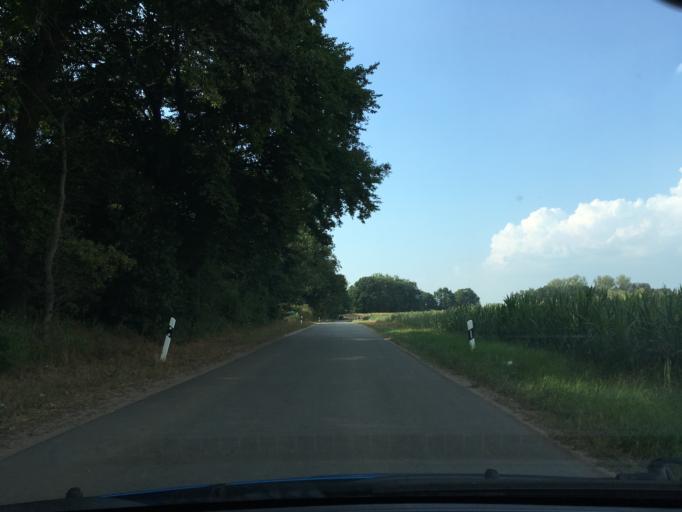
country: DE
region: Lower Saxony
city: Damnatz
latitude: 53.1450
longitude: 11.1214
